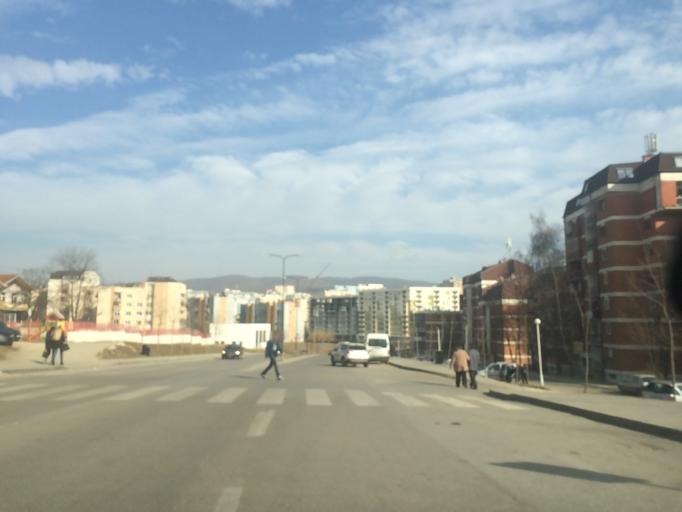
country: XK
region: Pristina
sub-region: Komuna e Prishtines
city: Pristina
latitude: 42.6524
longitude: 21.1722
